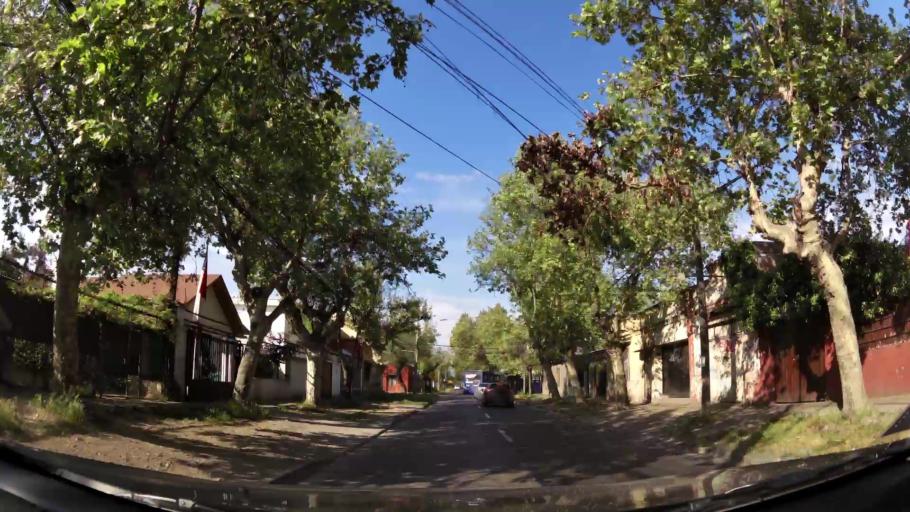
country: CL
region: Santiago Metropolitan
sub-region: Provincia de Maipo
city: San Bernardo
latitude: -33.5981
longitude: -70.7015
